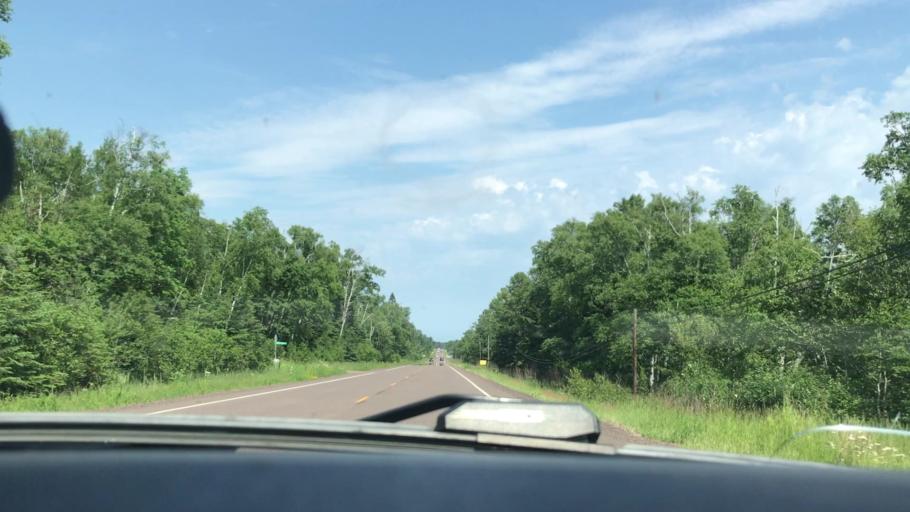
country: US
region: Minnesota
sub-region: Cook County
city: Grand Marais
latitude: 47.6420
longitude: -90.6961
